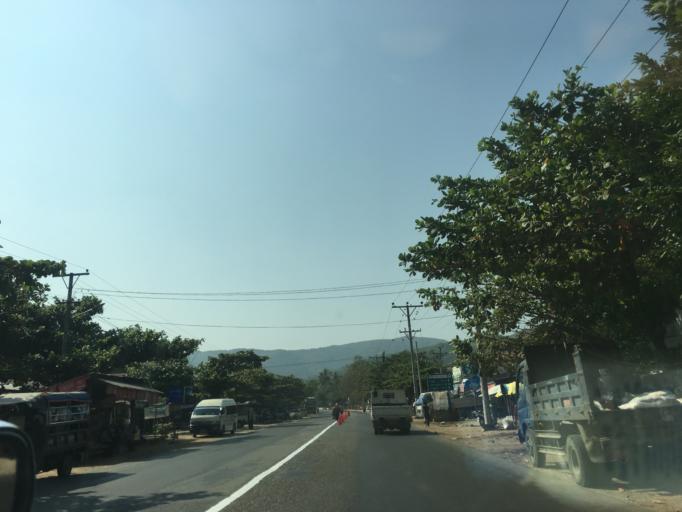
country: MM
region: Mon
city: Martaban
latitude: 16.6064
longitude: 97.5254
